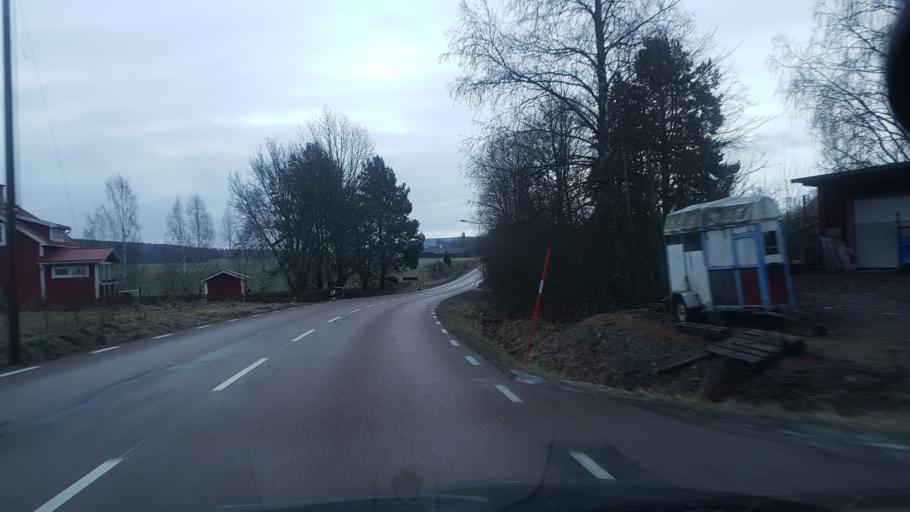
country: SE
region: Dalarna
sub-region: Saters Kommun
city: Saeter
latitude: 60.4157
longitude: 15.7856
